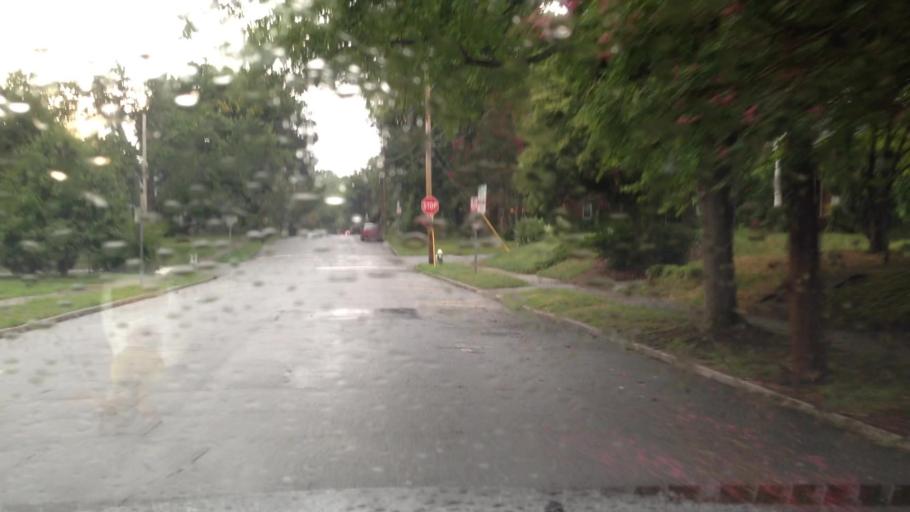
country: US
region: North Carolina
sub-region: Guilford County
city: Greensboro
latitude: 36.0658
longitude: -79.8169
